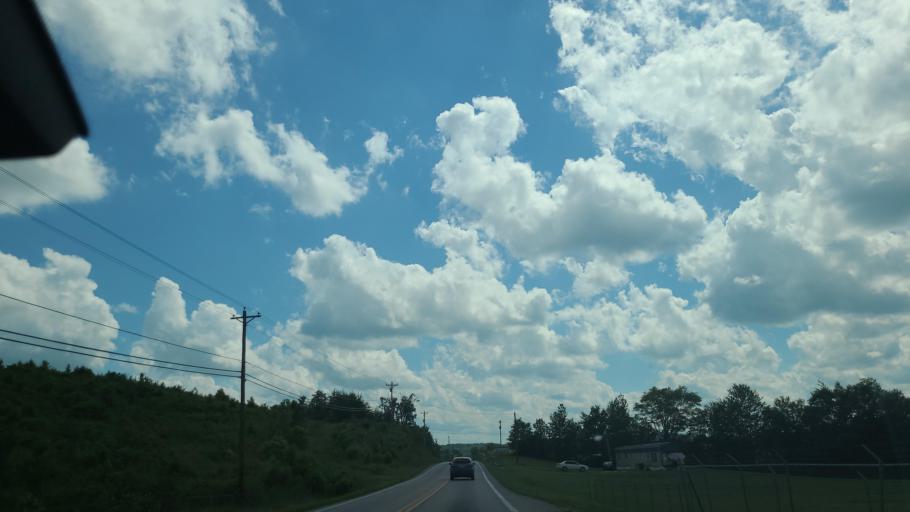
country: US
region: Kentucky
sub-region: Whitley County
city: Corbin
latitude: 36.8943
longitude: -84.1842
